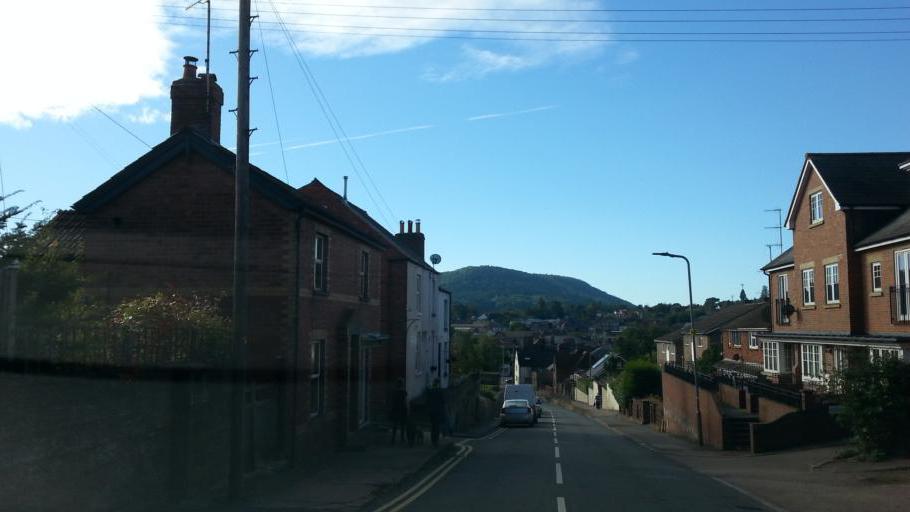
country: GB
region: England
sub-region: Herefordshire
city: Ross on Wye
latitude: 51.9190
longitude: -2.5812
